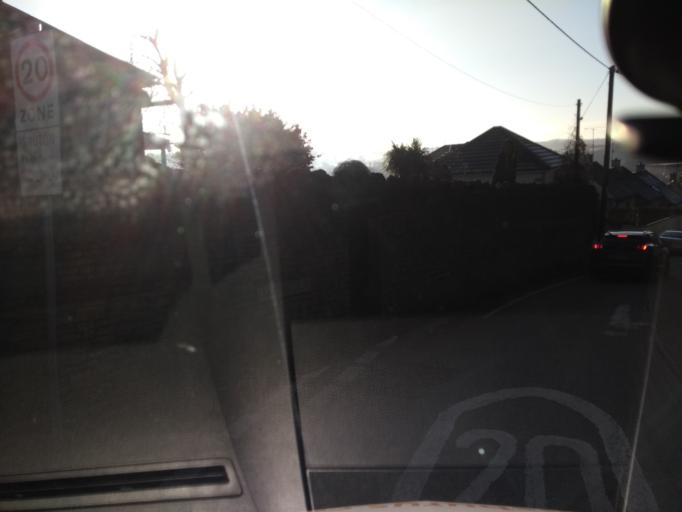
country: GB
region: England
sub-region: Somerset
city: Bruton
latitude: 51.1154
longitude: -2.4534
